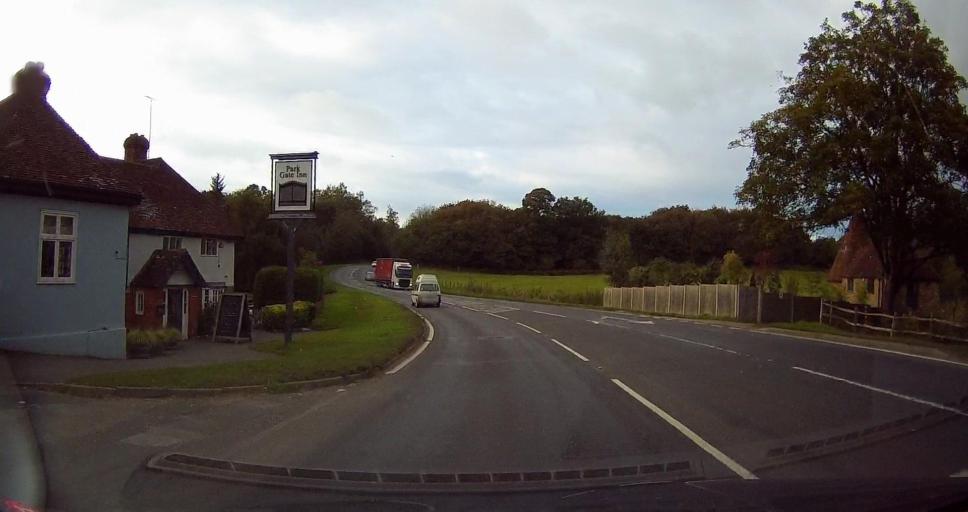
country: GB
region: England
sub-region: Kent
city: Harrietsham
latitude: 51.2531
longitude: 0.6338
